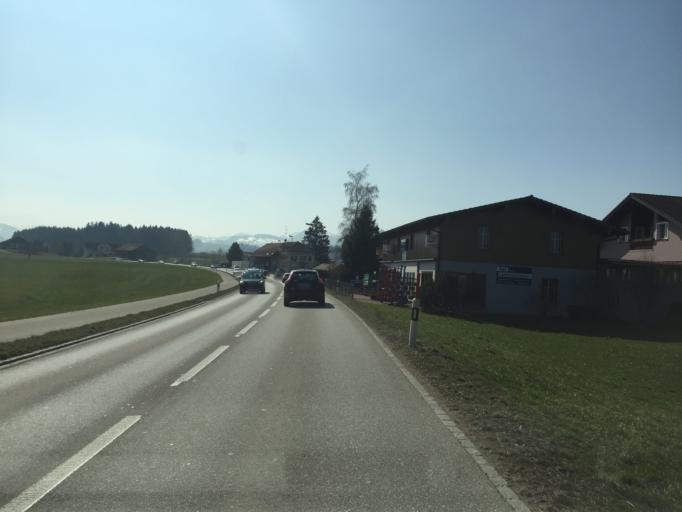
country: CH
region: Saint Gallen
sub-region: Wahlkreis Toggenburg
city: Lutisburg
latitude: 47.3849
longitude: 9.0727
